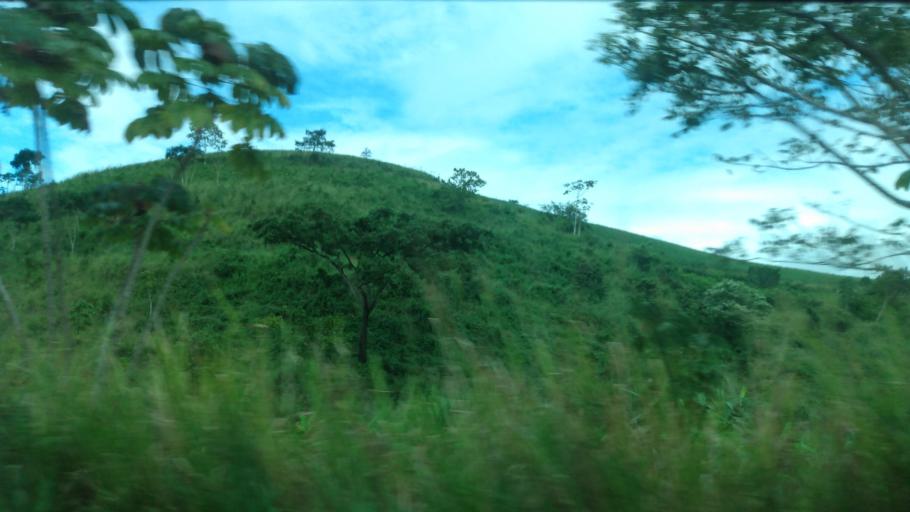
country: BR
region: Pernambuco
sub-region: Catende
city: Catende
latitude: -8.7113
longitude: -35.7692
